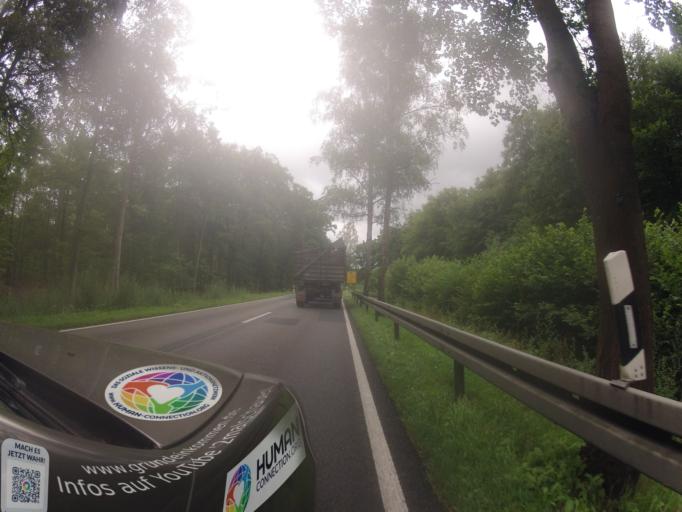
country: DE
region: Mecklenburg-Vorpommern
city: Jatznick
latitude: 53.6051
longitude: 13.9396
